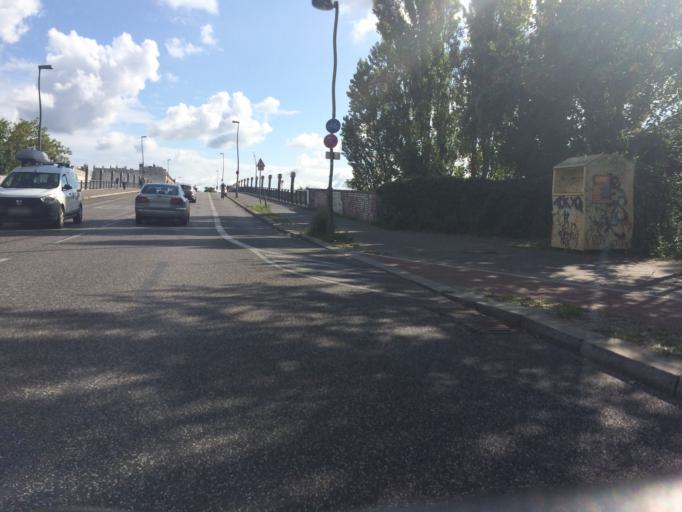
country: DE
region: Berlin
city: Gesundbrunnen
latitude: 52.5508
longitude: 13.3964
